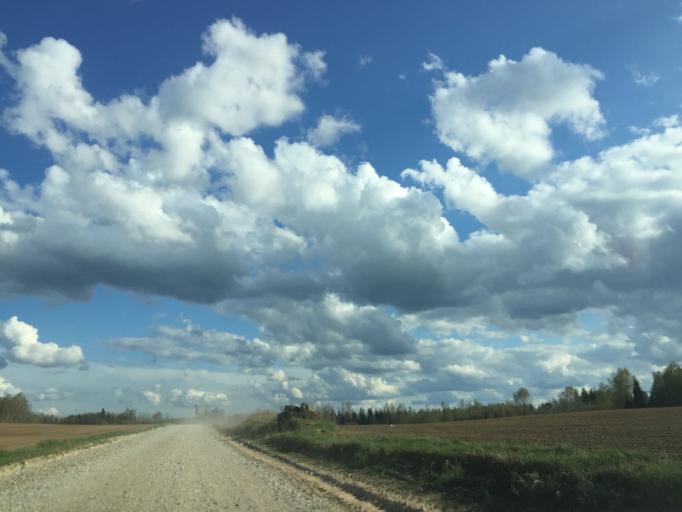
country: LV
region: Beverina
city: Murmuiza
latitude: 57.3905
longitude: 25.4808
